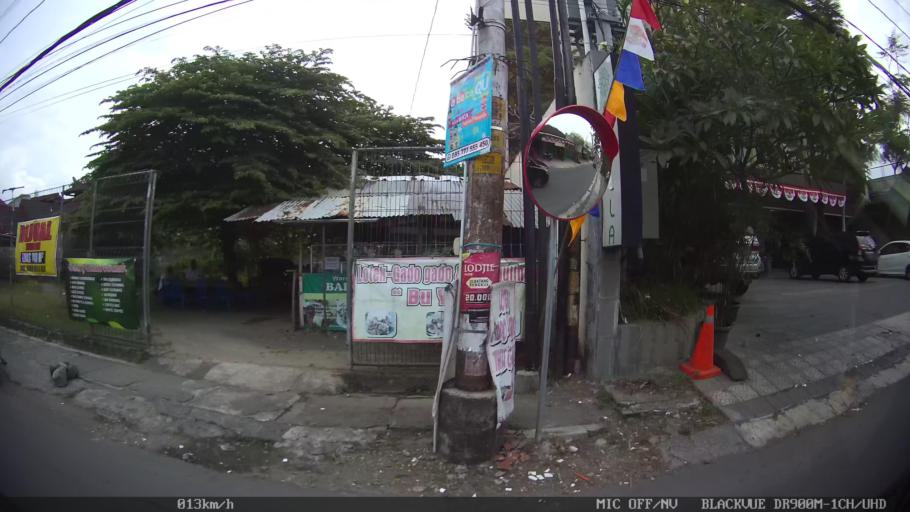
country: ID
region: Daerah Istimewa Yogyakarta
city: Yogyakarta
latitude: -7.7868
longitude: 110.3996
